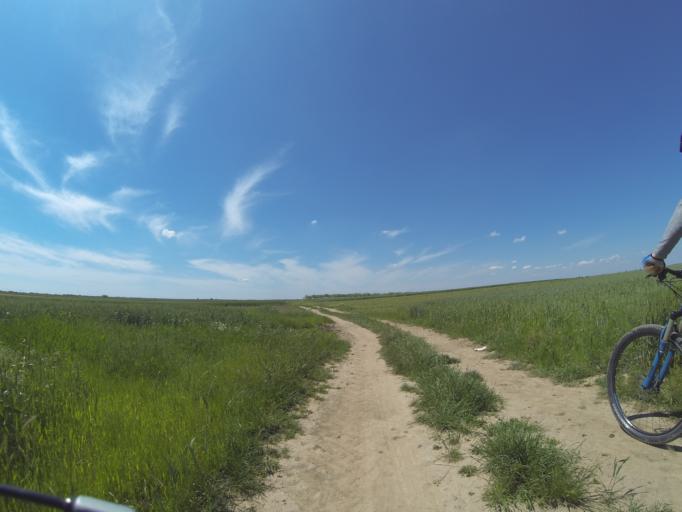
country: RO
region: Dolj
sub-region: Comuna Leu
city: Leu
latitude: 44.2191
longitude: 24.0116
